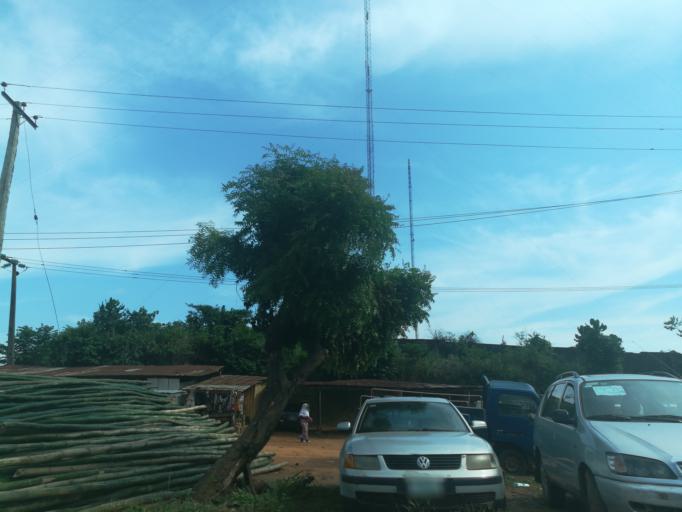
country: NG
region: Lagos
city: Ikorodu
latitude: 6.6312
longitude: 3.5282
